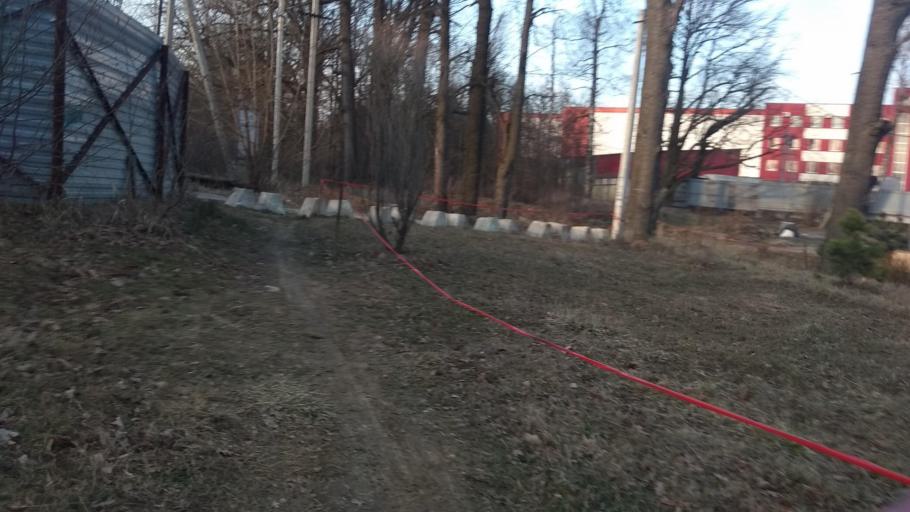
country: RU
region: Moskovskaya
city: Razvilka
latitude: 55.5648
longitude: 37.7418
